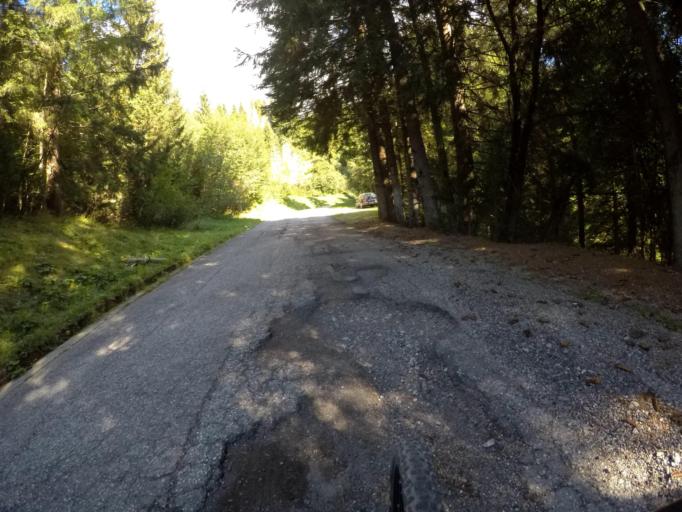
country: IT
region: Friuli Venezia Giulia
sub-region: Provincia di Udine
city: Ligosullo
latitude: 46.5459
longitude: 13.0862
